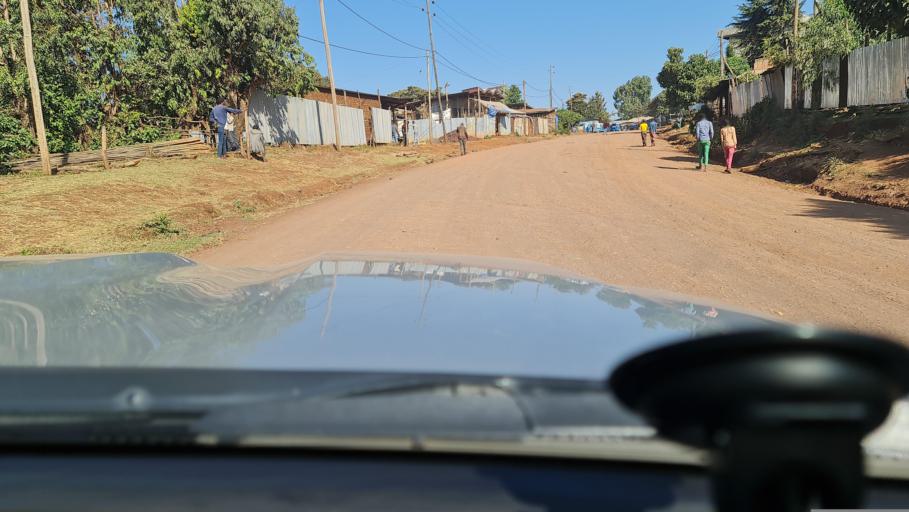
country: ET
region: Oromiya
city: Waliso
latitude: 8.6064
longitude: 37.9241
